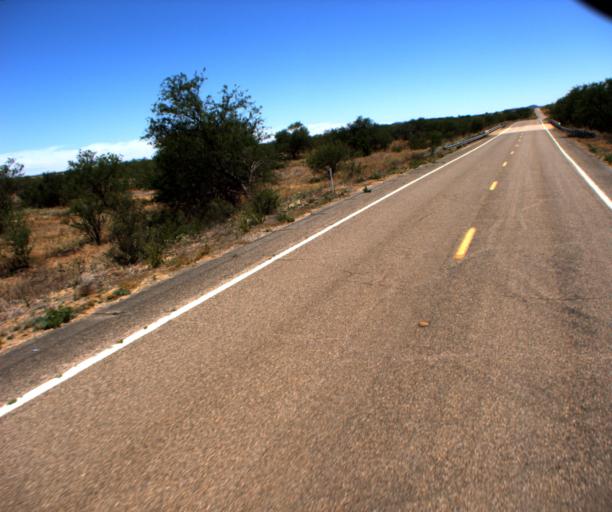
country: US
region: Arizona
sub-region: Pima County
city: Sells
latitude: 31.6038
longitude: -111.5231
